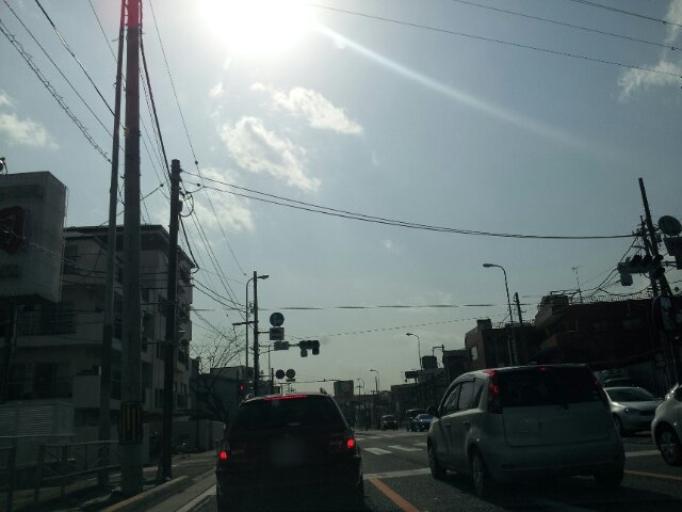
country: JP
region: Kanagawa
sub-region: Kawasaki-shi
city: Kawasaki
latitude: 35.5179
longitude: 139.6684
